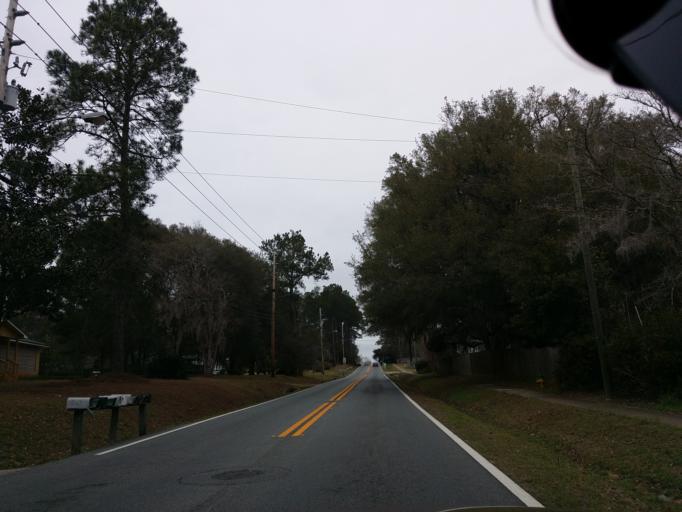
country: US
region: Florida
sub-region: Leon County
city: Tallahassee
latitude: 30.4926
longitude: -84.2299
